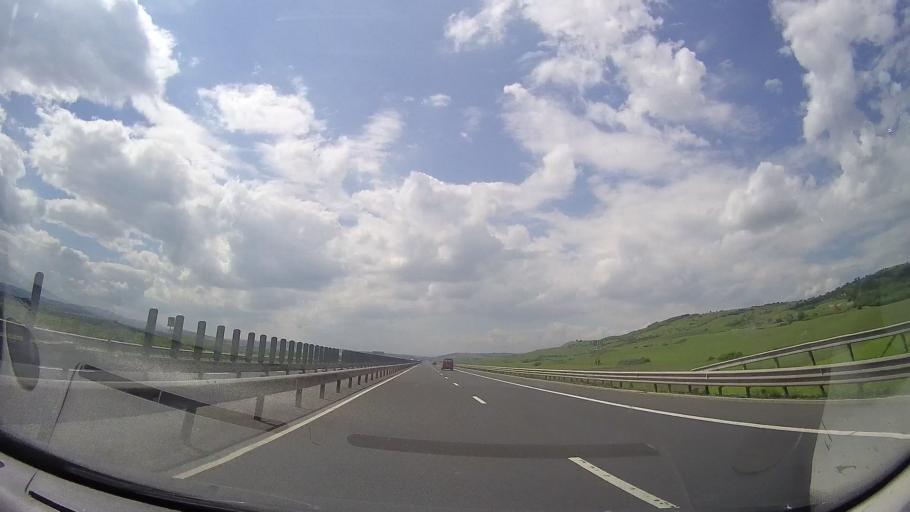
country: RO
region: Sibiu
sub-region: Comuna Apoldu de Jos
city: Apoldu de Jos
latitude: 45.8910
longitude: 23.8336
